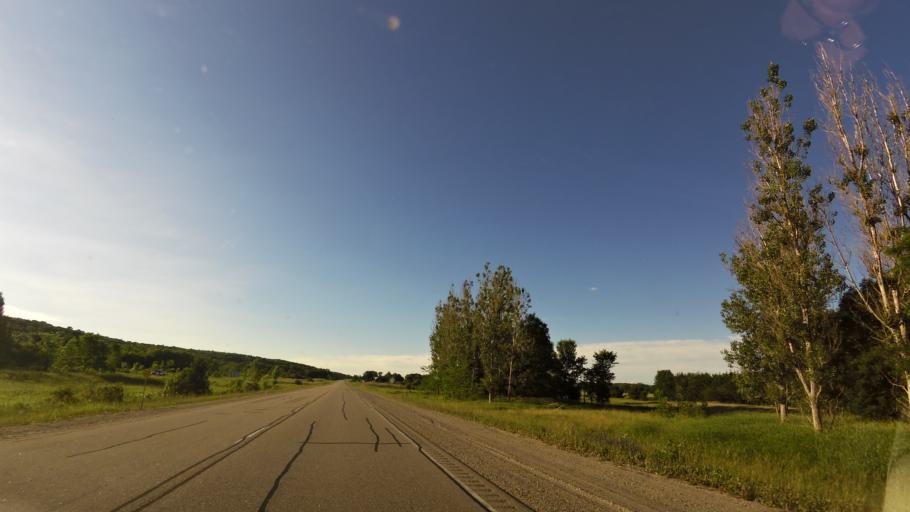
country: CA
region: Ontario
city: Orillia
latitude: 44.6732
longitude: -79.6441
